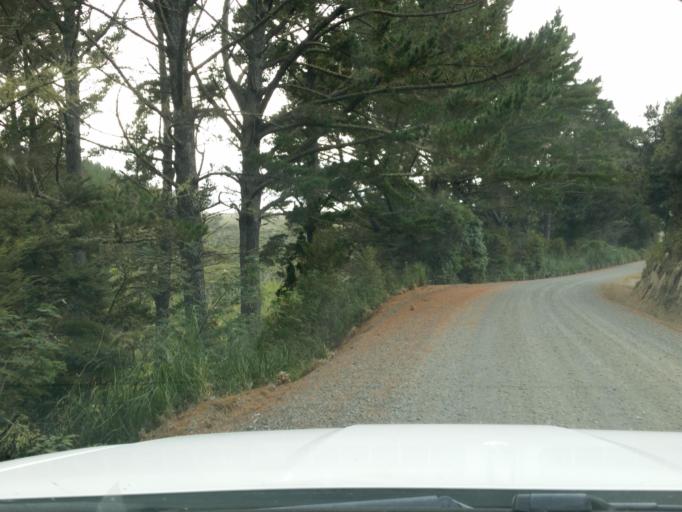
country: NZ
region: Northland
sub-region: Kaipara District
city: Dargaville
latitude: -36.2355
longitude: 174.0680
